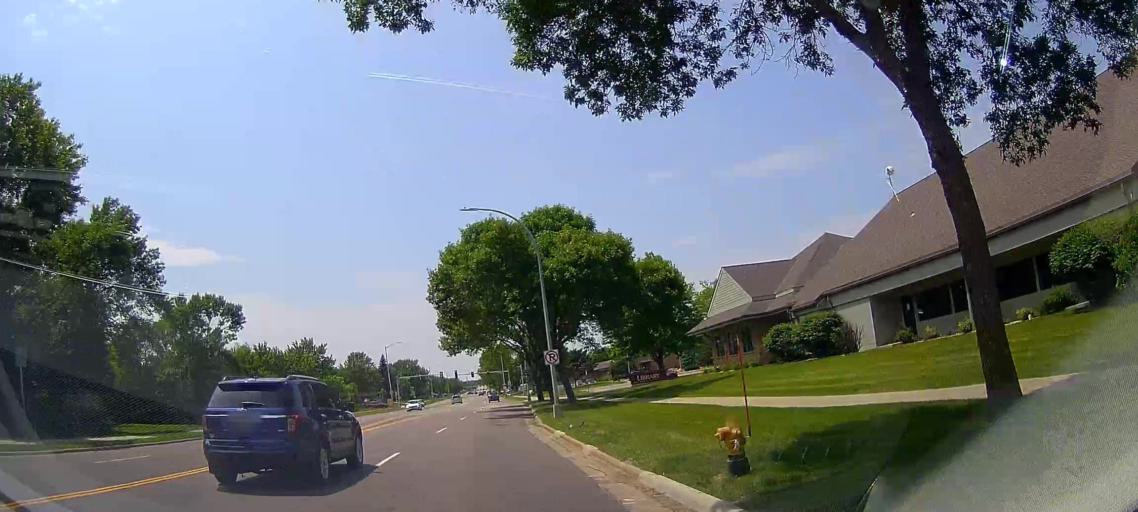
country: US
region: South Dakota
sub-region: Minnehaha County
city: Sioux Falls
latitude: 43.5076
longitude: -96.7643
